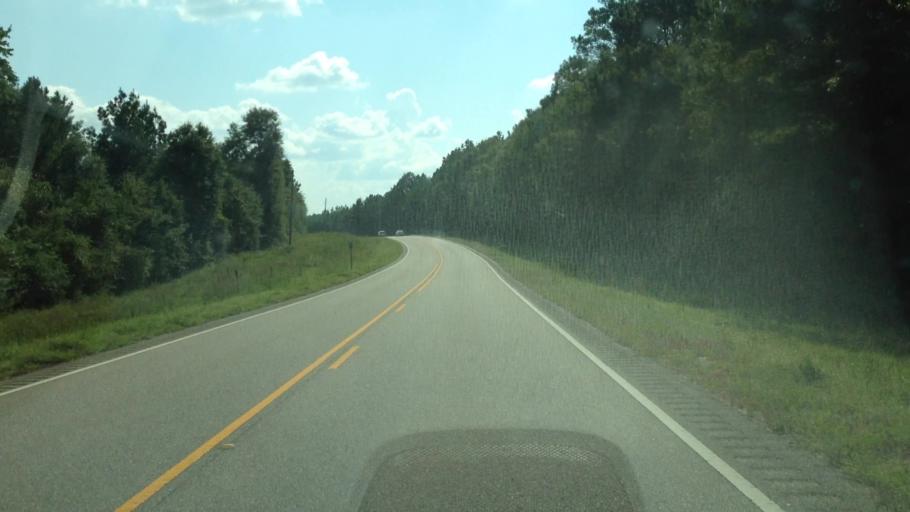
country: US
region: Florida
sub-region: Okaloosa County
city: Crestview
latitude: 31.0091
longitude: -86.6217
